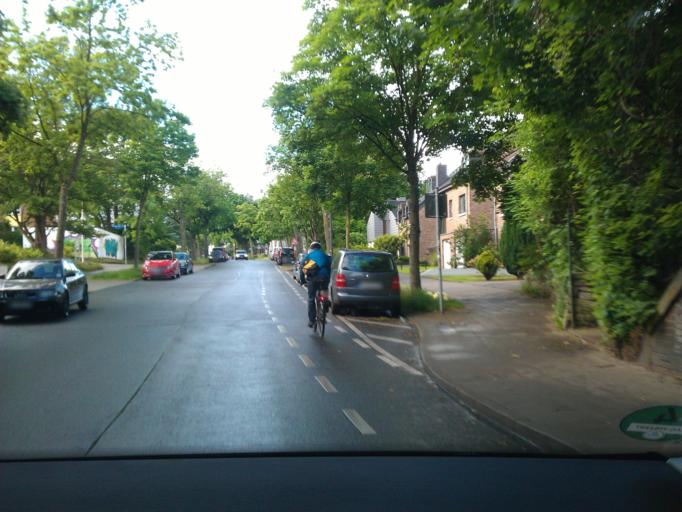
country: DE
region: North Rhine-Westphalia
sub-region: Regierungsbezirk Koln
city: Aachen
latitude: 50.7660
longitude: 6.1092
